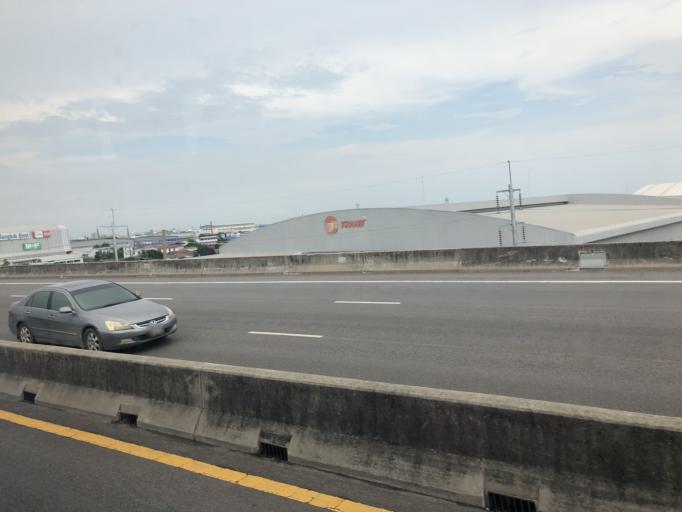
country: TH
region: Samut Prakan
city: Bang Bo District
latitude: 13.6071
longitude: 100.7704
